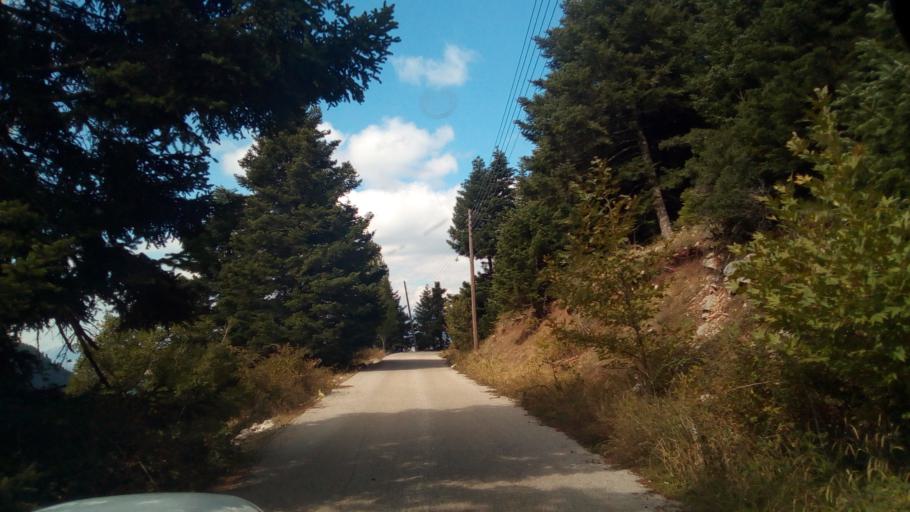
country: GR
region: West Greece
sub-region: Nomos Aitolias kai Akarnanias
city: Thermo
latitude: 38.6492
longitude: 21.9218
